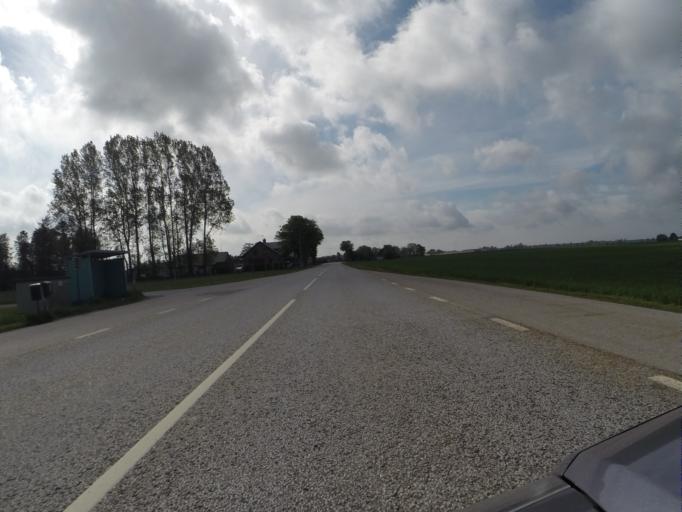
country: SE
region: Skane
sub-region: Svalovs Kommun
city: Teckomatorp
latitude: 55.8510
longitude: 13.0080
